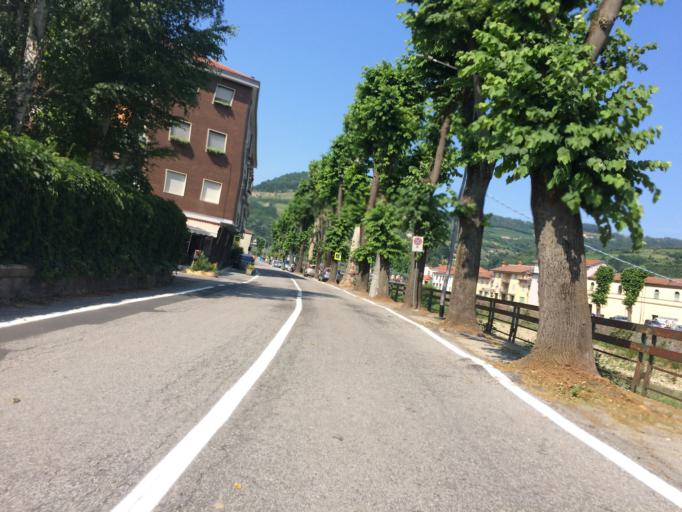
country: IT
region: Piedmont
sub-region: Provincia di Cuneo
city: Cortemilia
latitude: 44.5781
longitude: 8.1905
